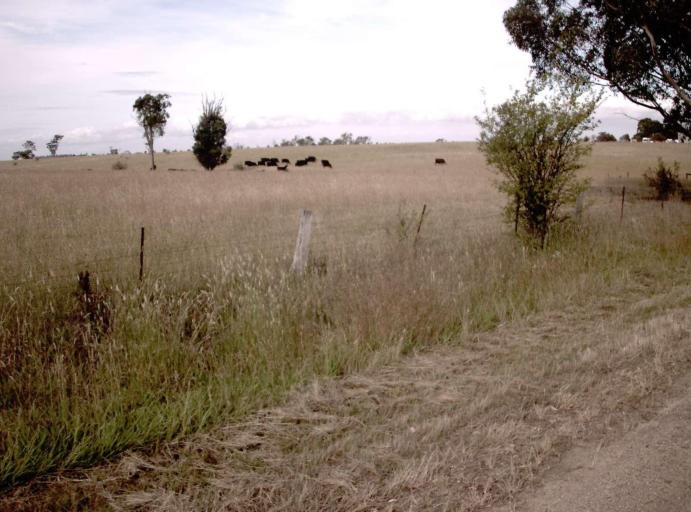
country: AU
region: Victoria
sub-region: Wellington
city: Heyfield
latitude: -37.9805
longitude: 146.8003
